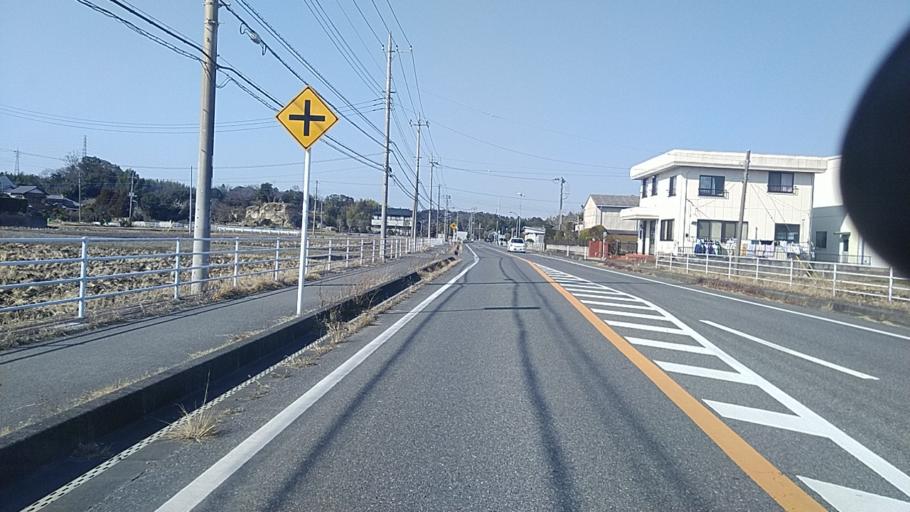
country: JP
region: Chiba
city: Mobara
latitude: 35.4576
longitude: 140.2874
